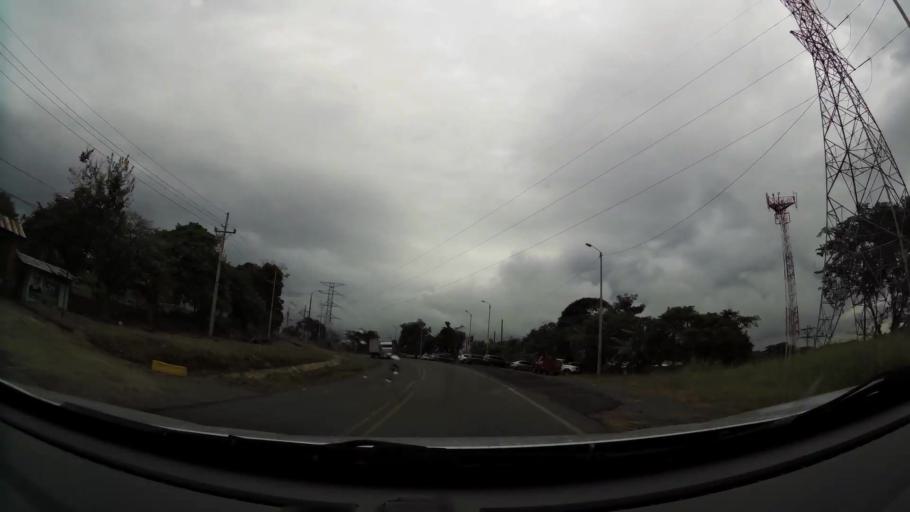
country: CR
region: Puntarenas
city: Esparza
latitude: 9.9931
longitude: -84.7070
